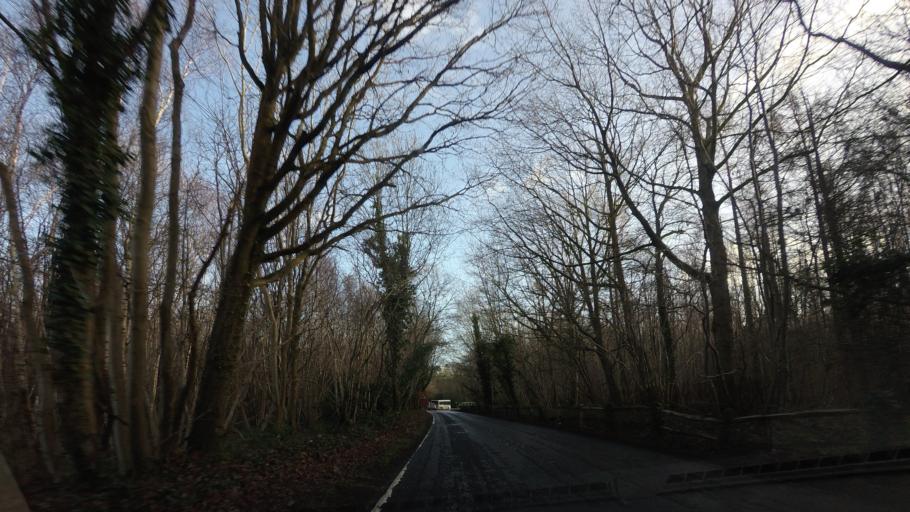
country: GB
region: England
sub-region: Kent
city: Tonbridge
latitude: 51.2297
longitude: 0.2919
